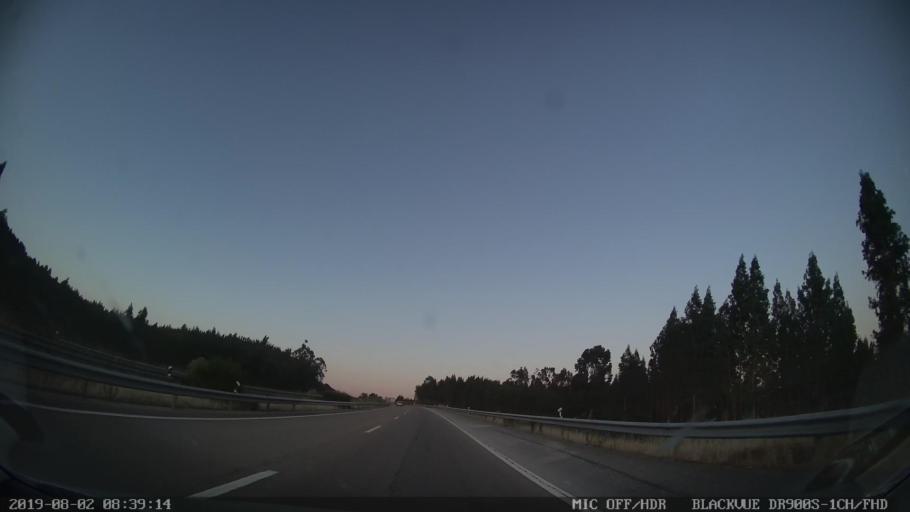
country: PT
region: Santarem
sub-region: Constancia
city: Constancia
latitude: 39.4892
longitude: -8.3163
